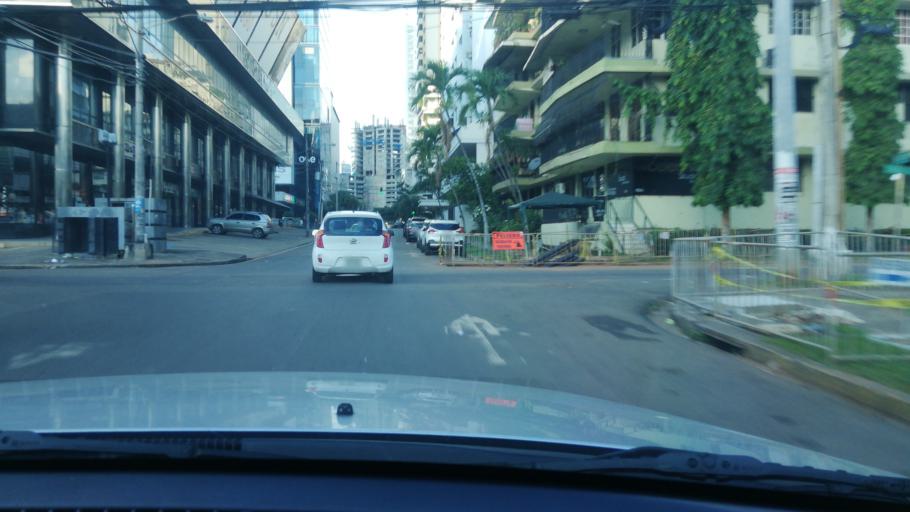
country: PA
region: Panama
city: Panama
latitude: 8.9885
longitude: -79.5196
